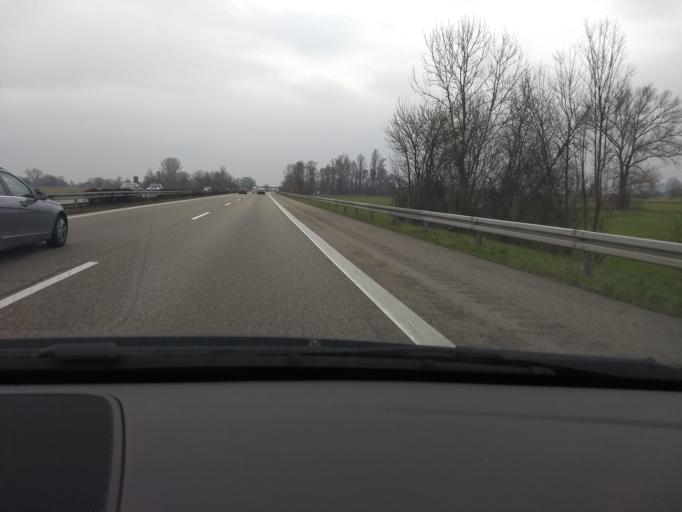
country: DE
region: Baden-Wuerttemberg
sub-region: Freiburg Region
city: Kenzingen
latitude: 48.2071
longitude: 7.7459
